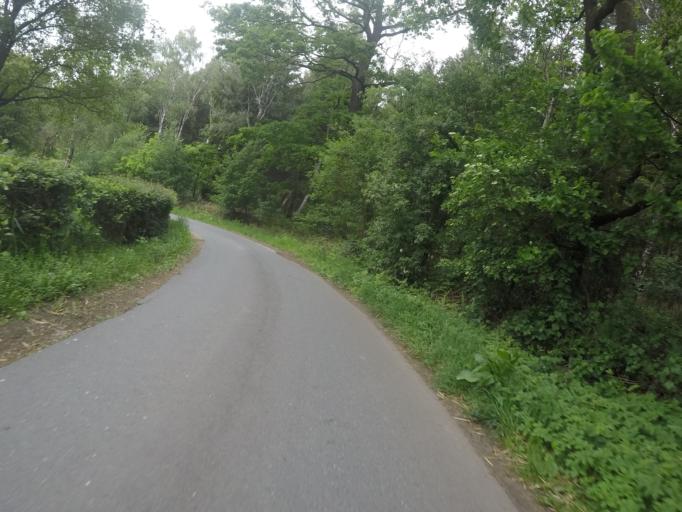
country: DE
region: Schleswig-Holstein
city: Bonningstedt
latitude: 53.6590
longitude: 9.9392
